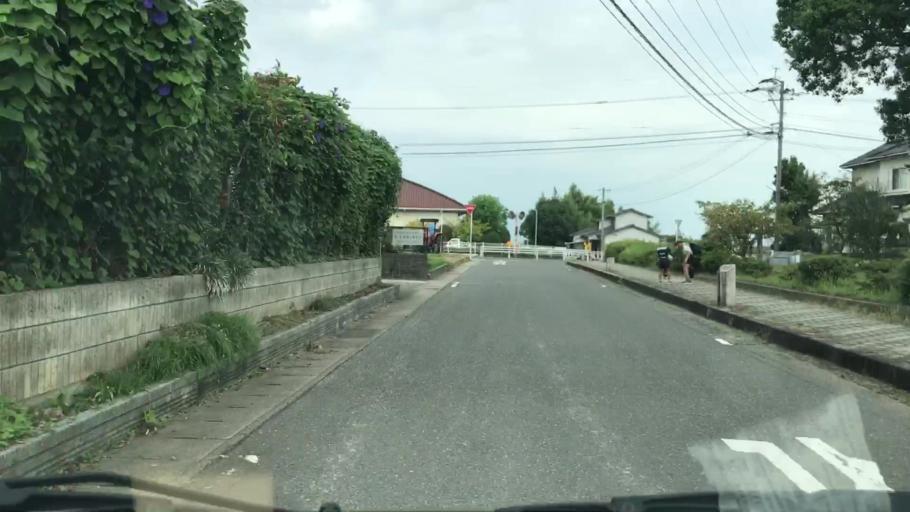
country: JP
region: Saga Prefecture
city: Saga-shi
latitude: 33.2812
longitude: 130.2259
